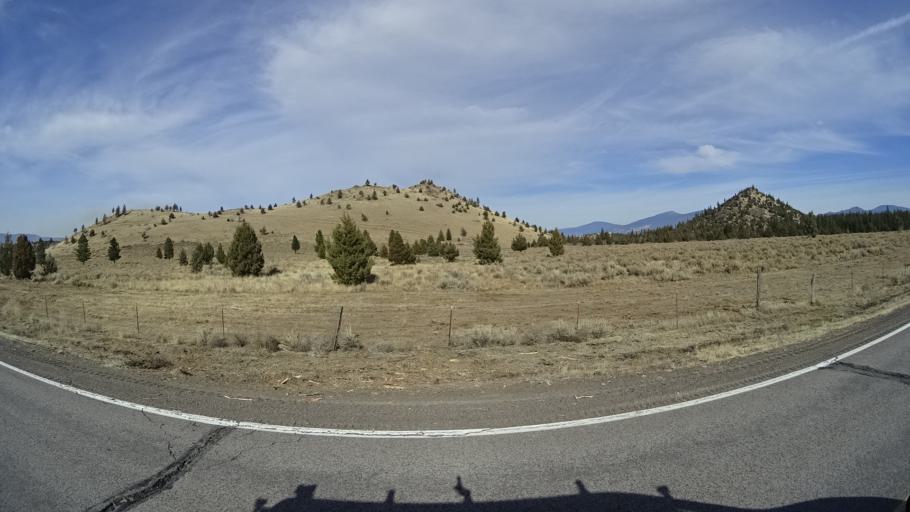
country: US
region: California
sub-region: Siskiyou County
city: Weed
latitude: 41.4940
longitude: -122.3925
